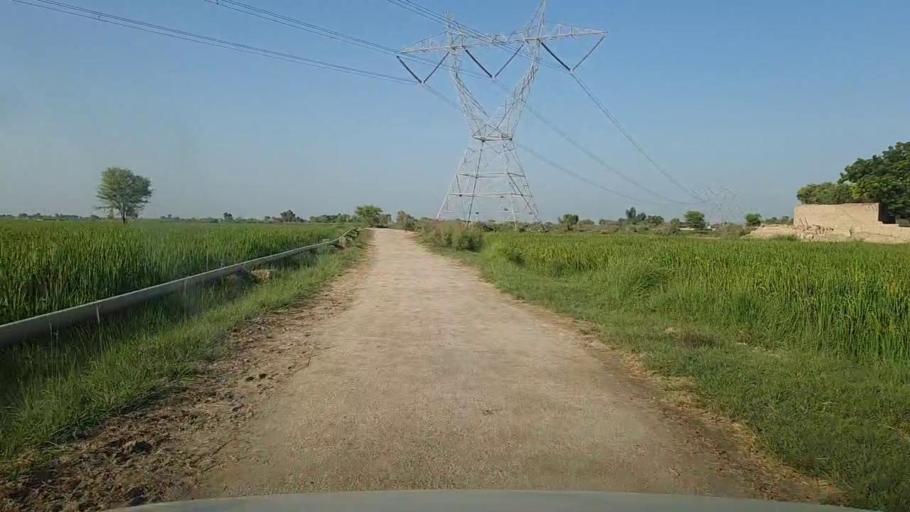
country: PK
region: Sindh
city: Kandhkot
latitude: 28.2947
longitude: 69.3262
